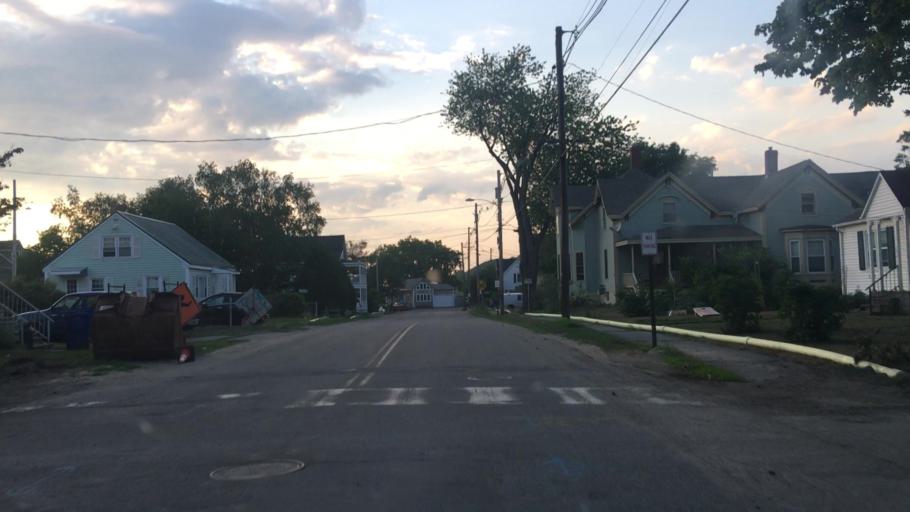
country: US
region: Maine
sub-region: Cumberland County
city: South Portland
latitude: 43.6340
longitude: -70.2691
